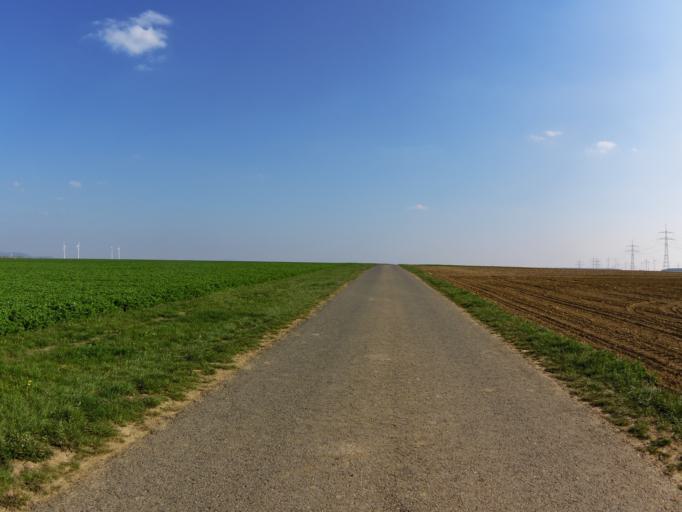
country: DE
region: Bavaria
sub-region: Regierungsbezirk Unterfranken
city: Biebelried
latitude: 49.7718
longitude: 10.0544
